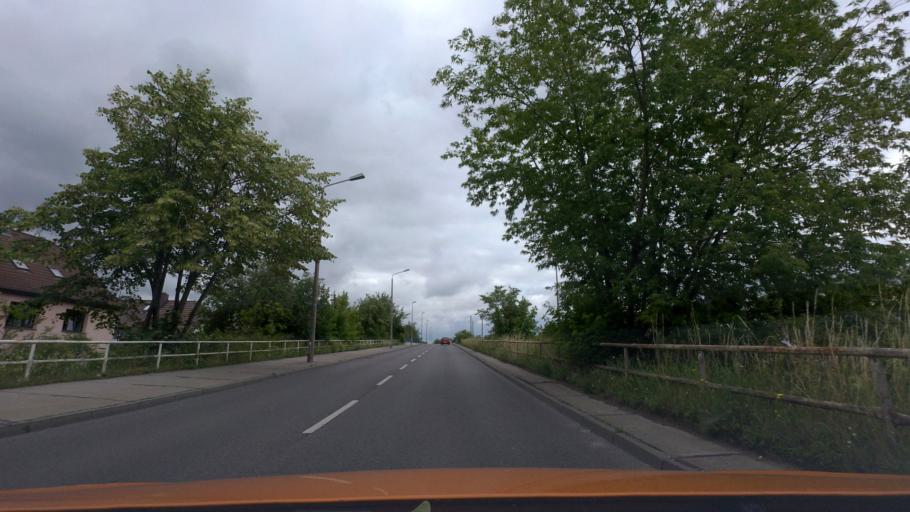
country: DE
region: Berlin
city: Neu-Hohenschoenhausen
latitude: 52.5546
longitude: 13.5231
